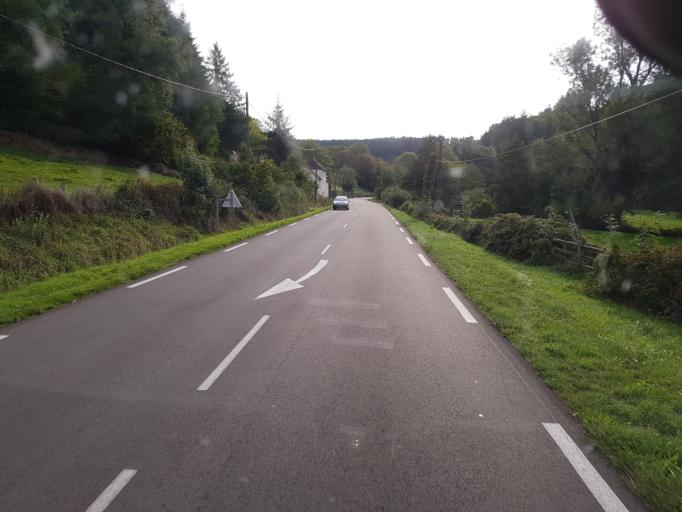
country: FR
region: Bourgogne
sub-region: Departement de Saone-et-Loire
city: Chauffailles
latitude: 46.2724
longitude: 4.3893
